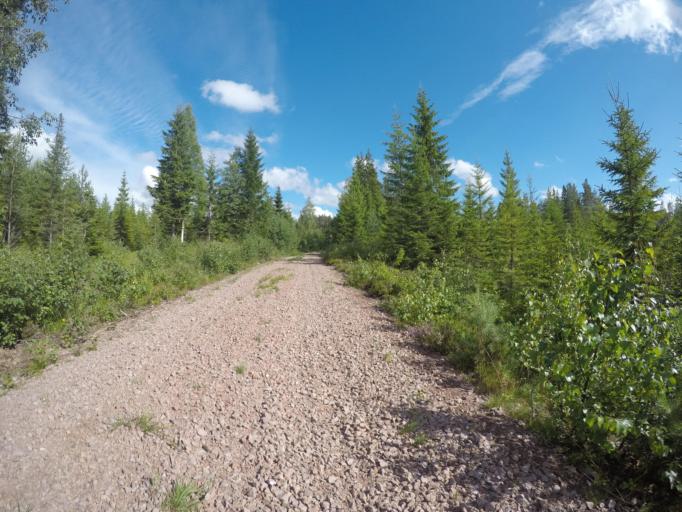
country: SE
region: OErebro
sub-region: Hallefors Kommun
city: Haellefors
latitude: 60.0254
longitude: 14.5696
